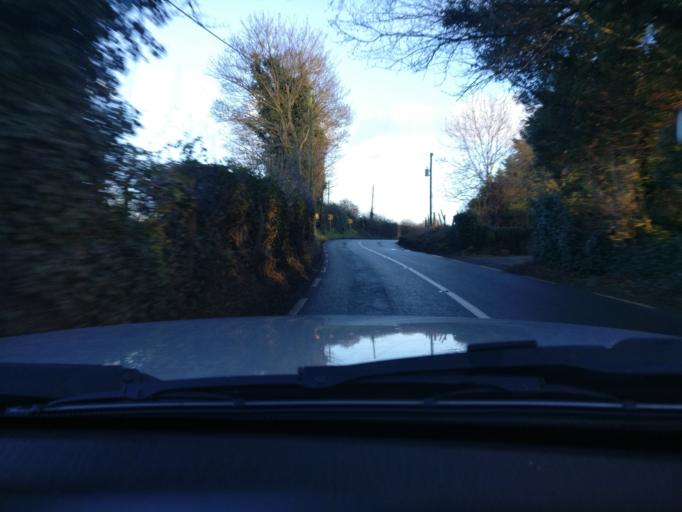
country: IE
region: Leinster
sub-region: An Mhi
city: Navan
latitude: 53.7970
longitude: -6.7065
